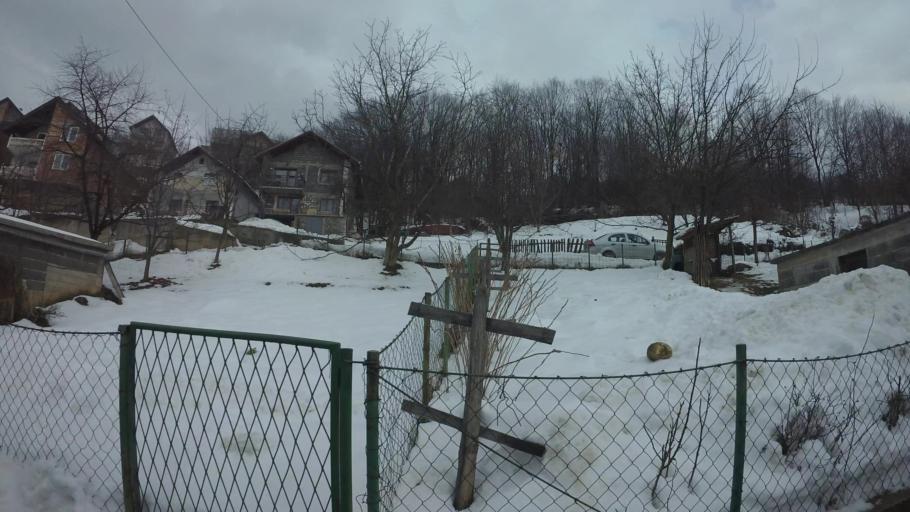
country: BA
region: Federation of Bosnia and Herzegovina
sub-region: Kanton Sarajevo
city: Sarajevo
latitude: 43.8615
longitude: 18.3519
